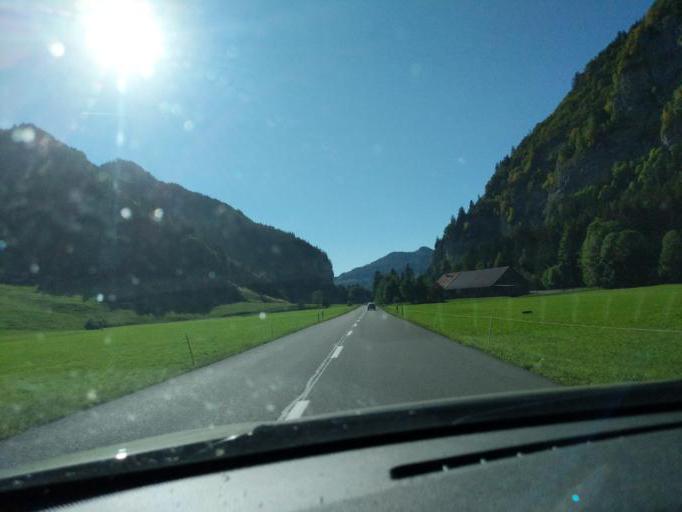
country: CH
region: Fribourg
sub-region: Gruyere District
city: Charmey
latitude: 46.6077
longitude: 7.1939
